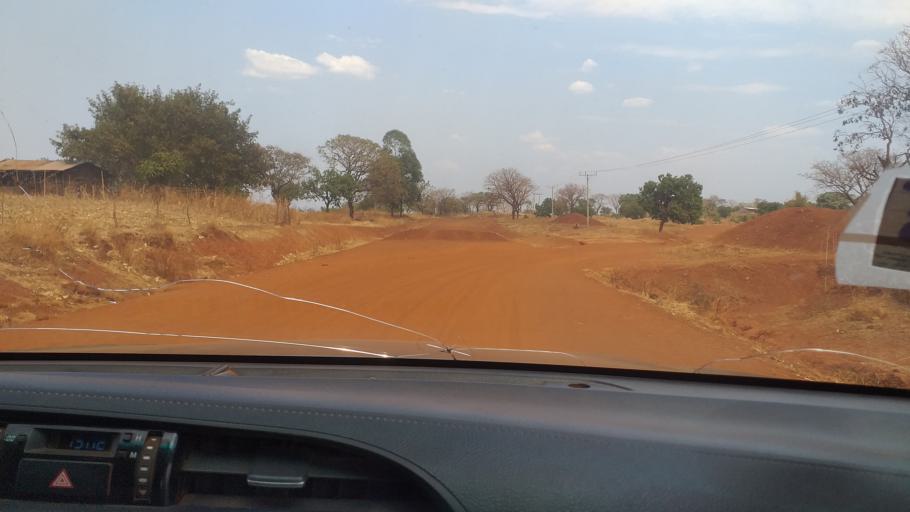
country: ET
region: Binshangul Gumuz
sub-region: Asosa
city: Asosa
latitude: 10.0620
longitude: 34.6985
